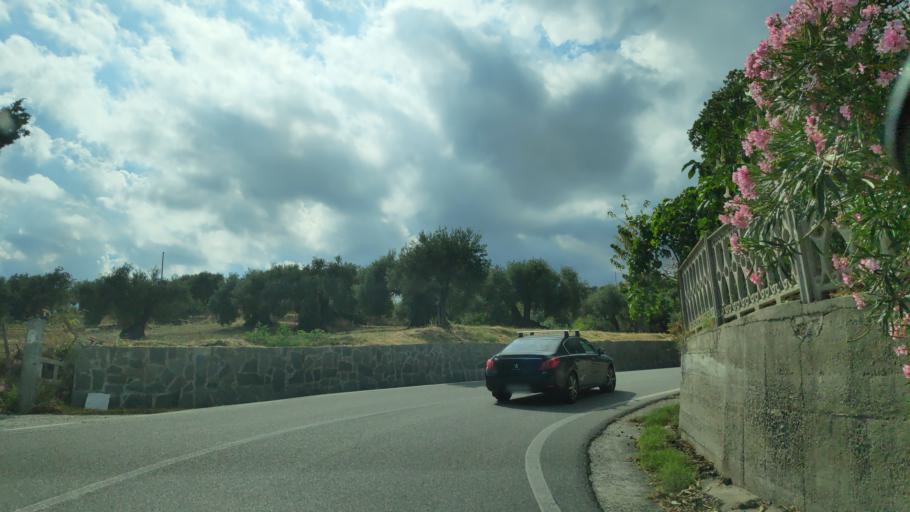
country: IT
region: Calabria
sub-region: Provincia di Catanzaro
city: Santa Caterina dello Ionio
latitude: 38.5254
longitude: 16.5307
